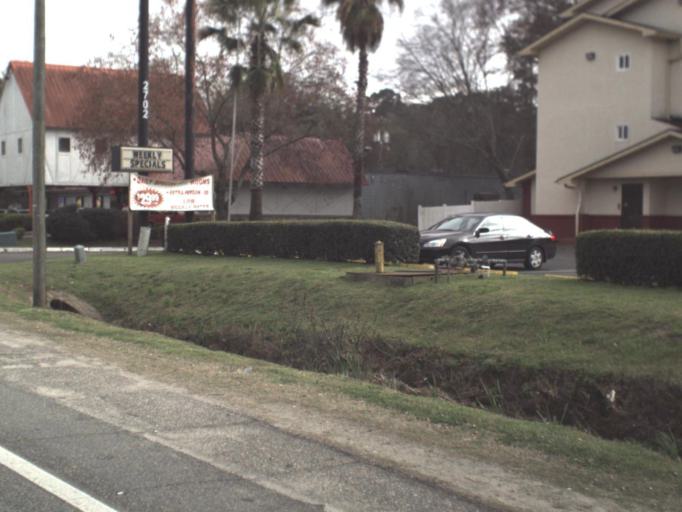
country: US
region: Florida
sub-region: Leon County
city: Tallahassee
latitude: 30.4781
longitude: -84.2998
